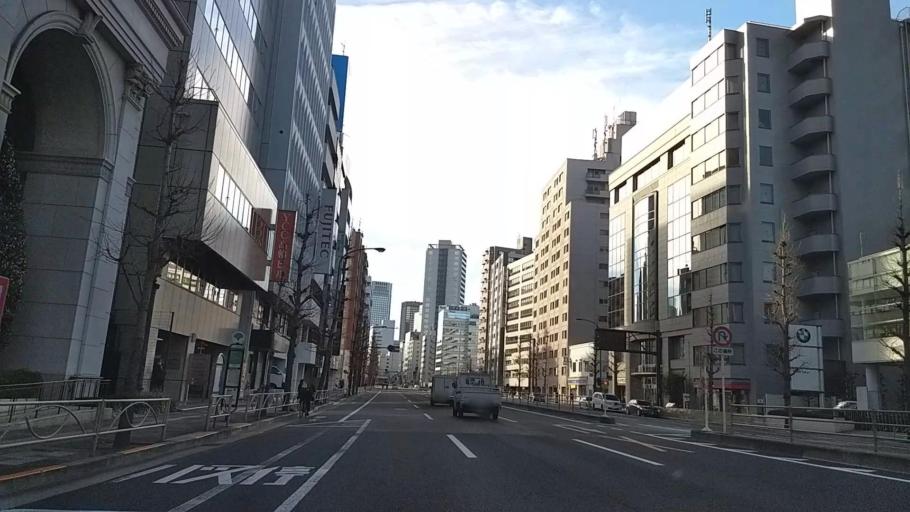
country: JP
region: Tokyo
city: Tokyo
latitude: 35.6369
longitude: 139.7392
